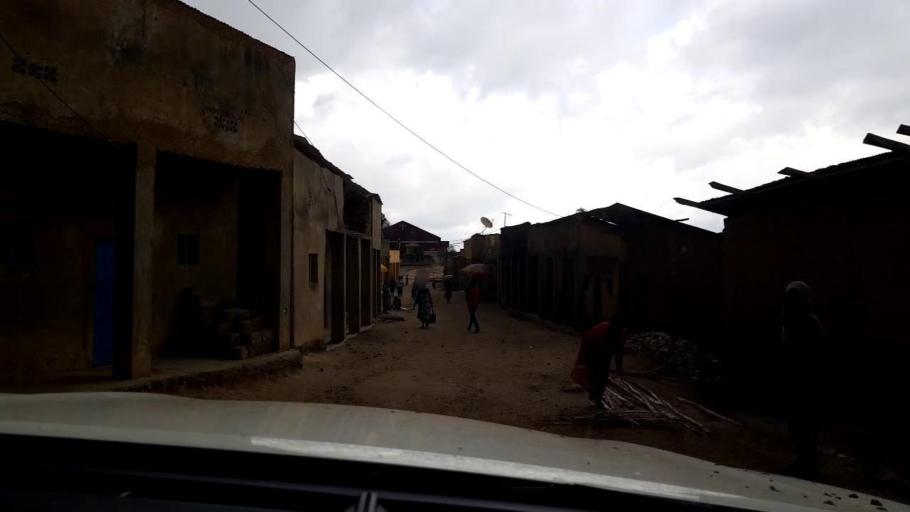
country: RW
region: Western Province
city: Kibuye
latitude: -1.8957
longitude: 29.5323
